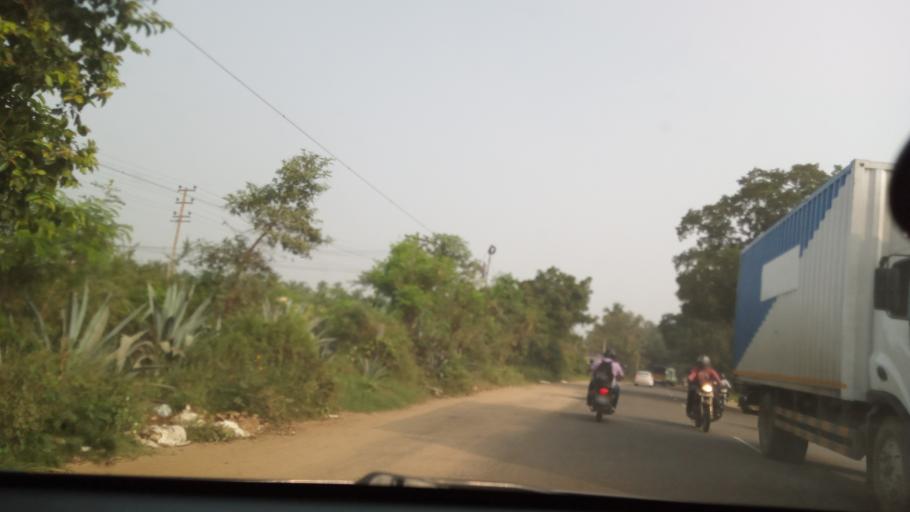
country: IN
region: Tamil Nadu
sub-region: Coimbatore
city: Annur
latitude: 11.1642
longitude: 77.0521
